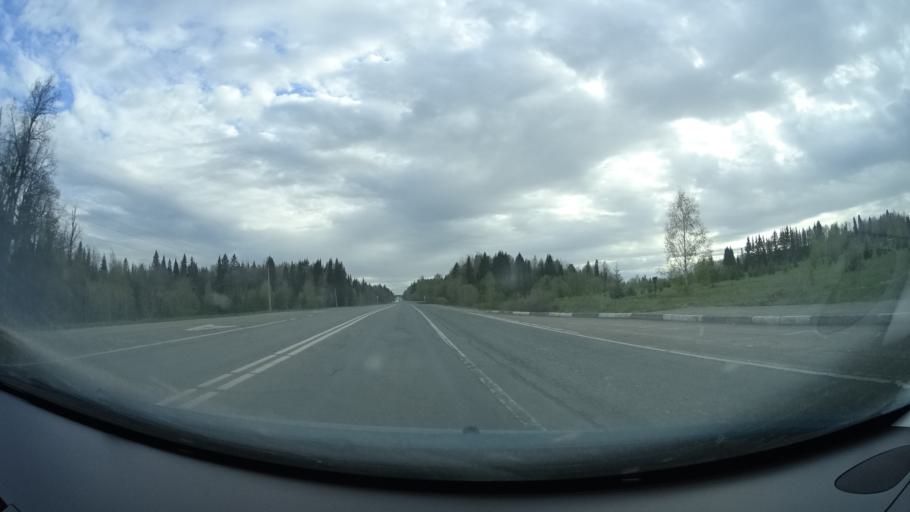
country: RU
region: Perm
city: Kultayevo
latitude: 57.8232
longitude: 55.8056
